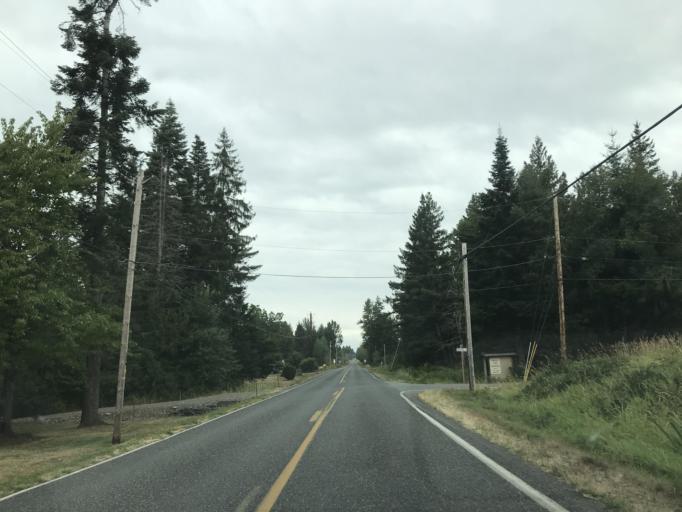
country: US
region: Washington
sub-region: Whatcom County
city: Everson
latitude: 48.8250
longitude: -122.3326
